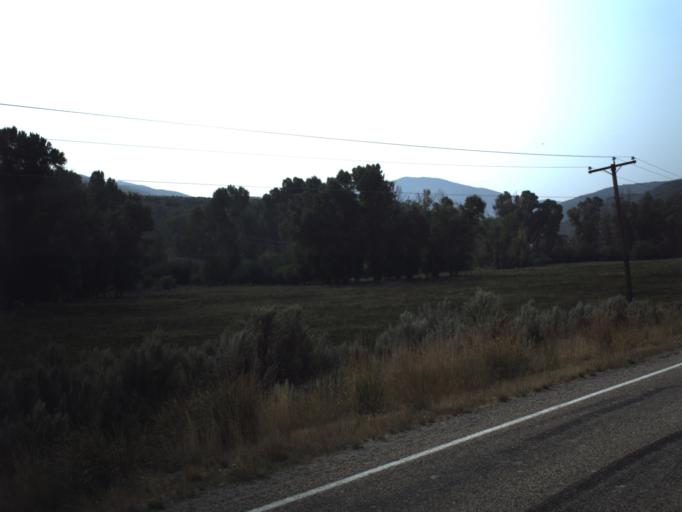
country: US
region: Utah
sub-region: Summit County
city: Summit Park
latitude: 40.8602
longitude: -111.5881
